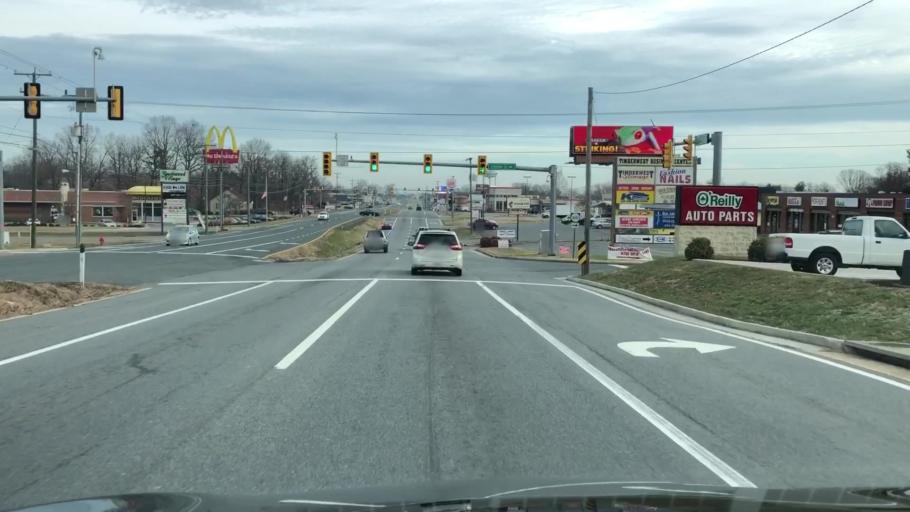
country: US
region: Virginia
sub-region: Campbell County
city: Timberlake
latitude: 37.3329
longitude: -79.2434
